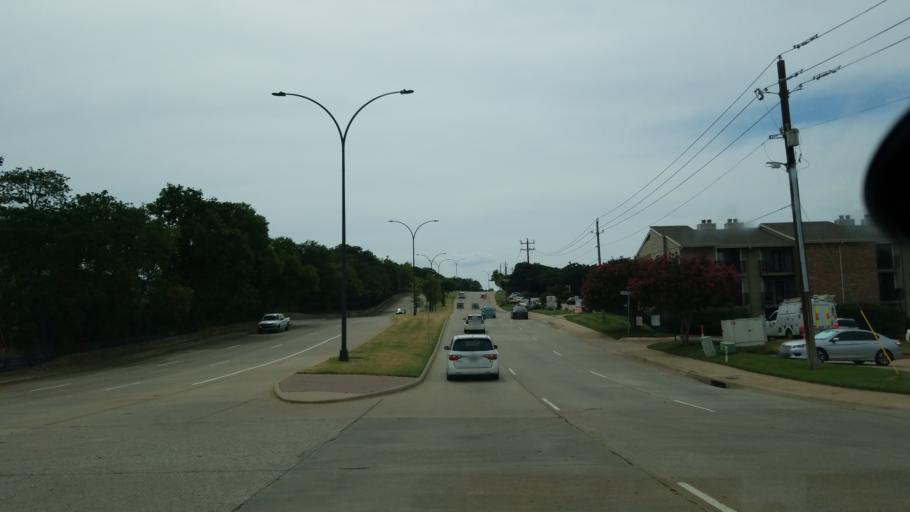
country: US
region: Texas
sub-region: Tarrant County
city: Arlington
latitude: 32.7847
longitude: -97.0970
